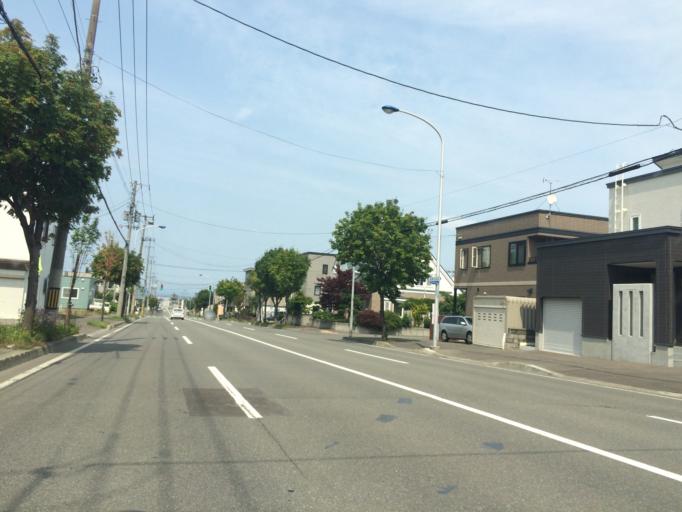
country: JP
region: Hokkaido
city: Sapporo
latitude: 43.0760
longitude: 141.2661
